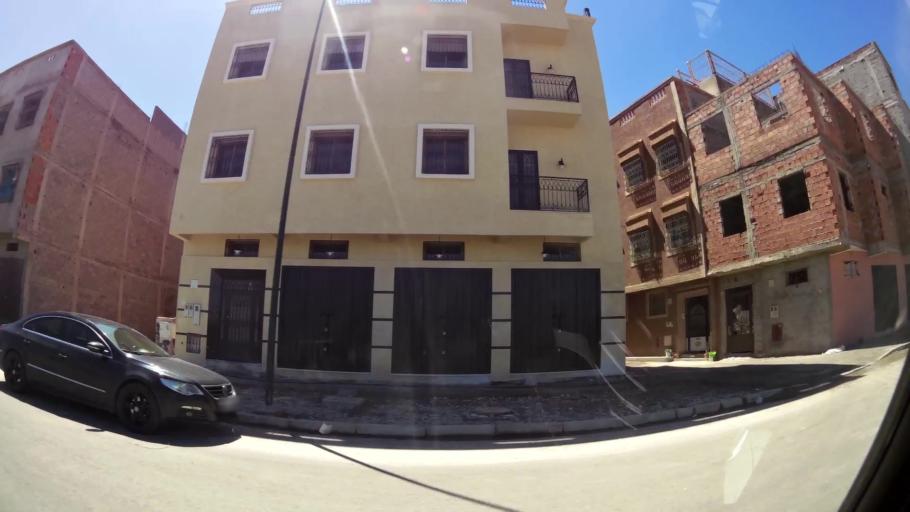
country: MA
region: Marrakech-Tensift-Al Haouz
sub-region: Marrakech
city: Marrakesh
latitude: 31.5549
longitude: -7.9792
